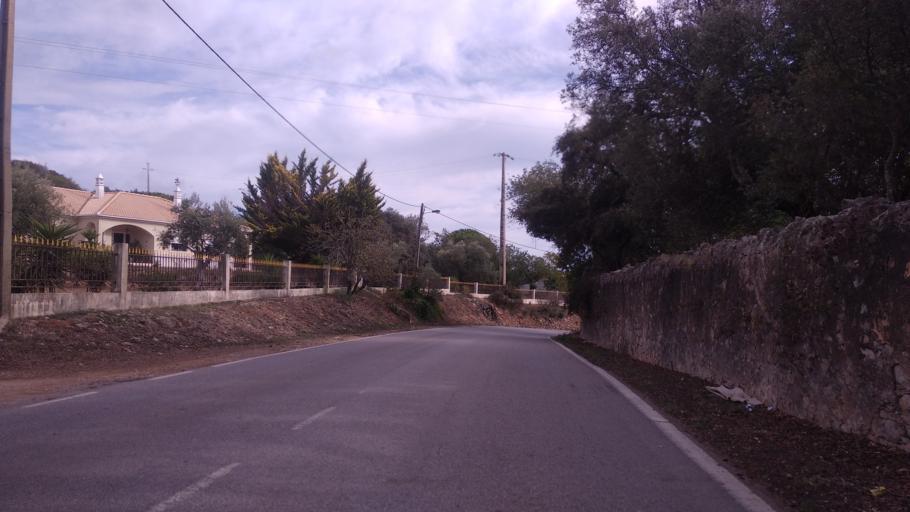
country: PT
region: Faro
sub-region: Sao Bras de Alportel
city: Sao Bras de Alportel
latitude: 37.1620
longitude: -7.9003
